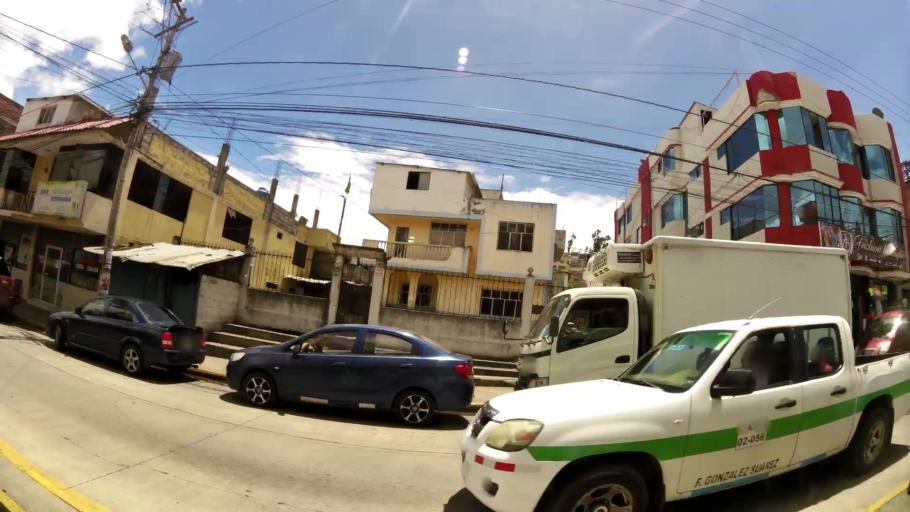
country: EC
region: Tungurahua
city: Pelileo
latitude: -1.3328
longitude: -78.5540
